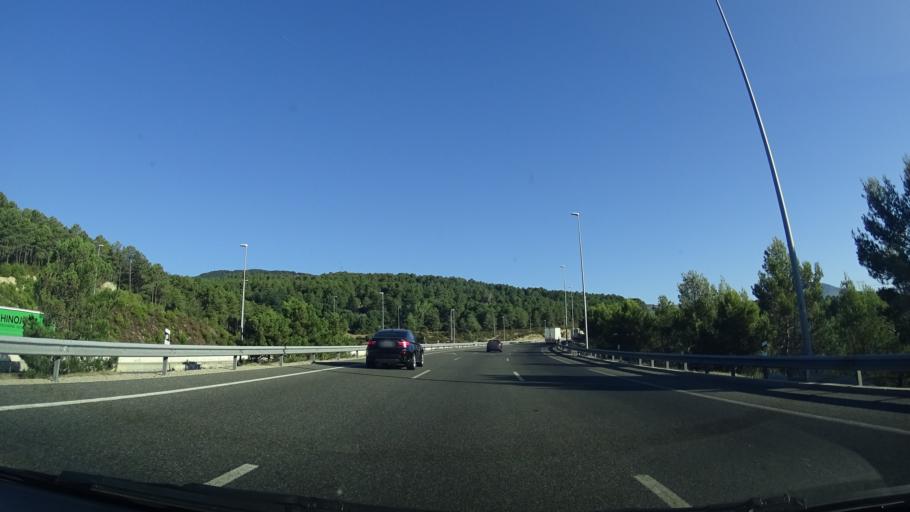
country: ES
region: Madrid
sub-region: Provincia de Madrid
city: Guadarrama
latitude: 40.6786
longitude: -4.1171
